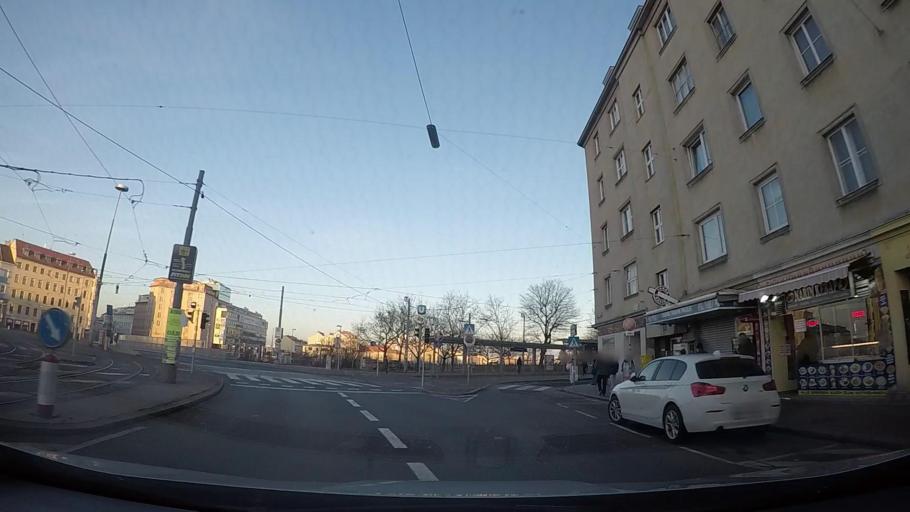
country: AT
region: Lower Austria
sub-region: Politischer Bezirk Modling
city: Vosendorf
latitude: 48.1732
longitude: 16.3296
